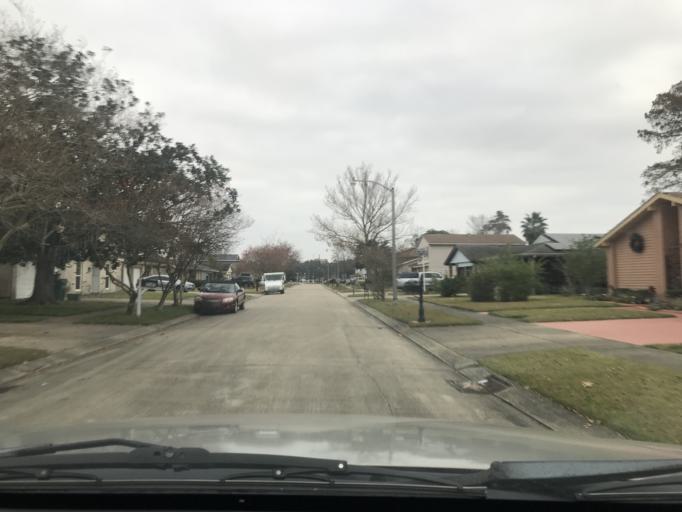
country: US
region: Louisiana
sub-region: Jefferson Parish
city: Woodmere
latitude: 29.8661
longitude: -90.0775
